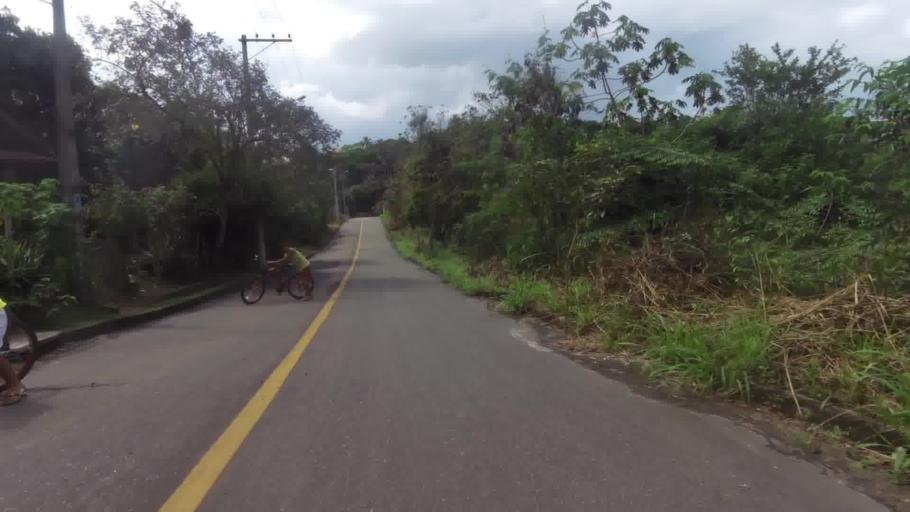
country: BR
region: Espirito Santo
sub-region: Piuma
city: Piuma
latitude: -20.8298
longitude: -40.7016
